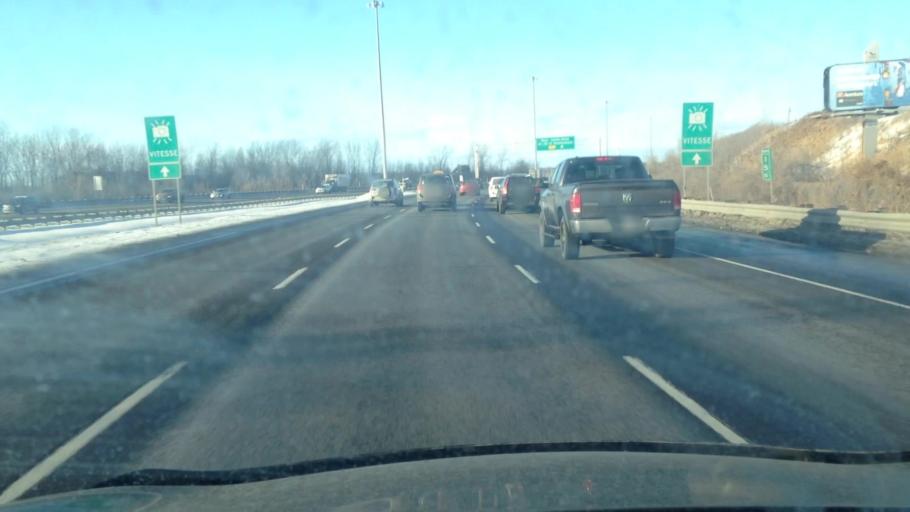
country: CA
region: Quebec
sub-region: Laurentides
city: Boisbriand
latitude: 45.5929
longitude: -73.8017
